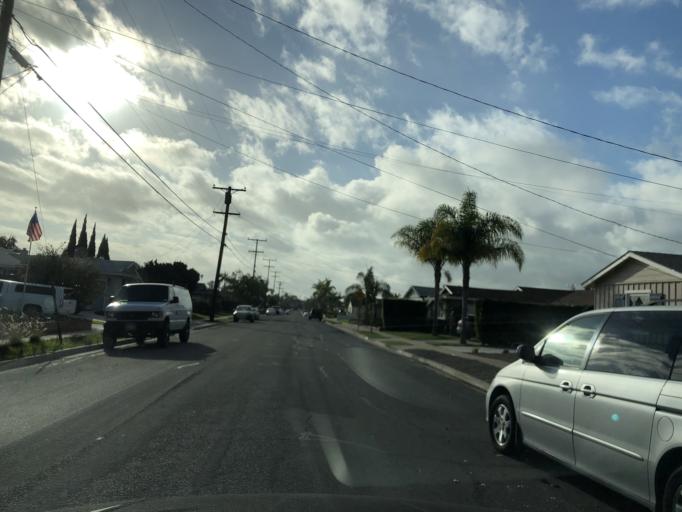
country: US
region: California
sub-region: San Diego County
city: La Jolla
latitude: 32.8190
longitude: -117.1861
